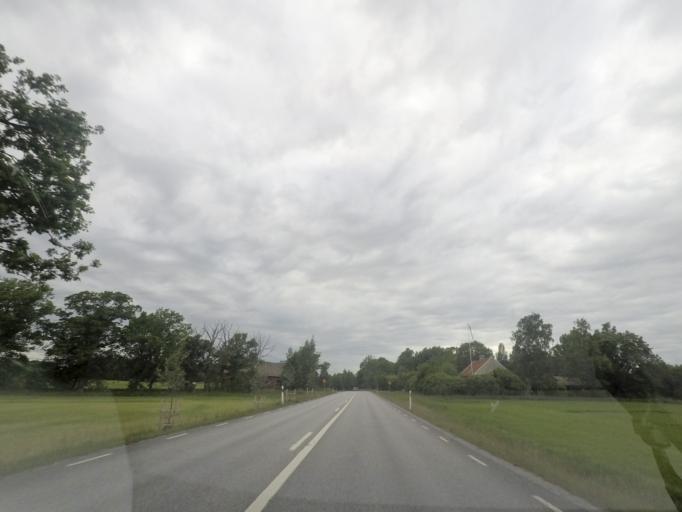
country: SE
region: Vaestmanland
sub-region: Arboga Kommun
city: Arboga
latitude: 59.4117
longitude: 15.7875
